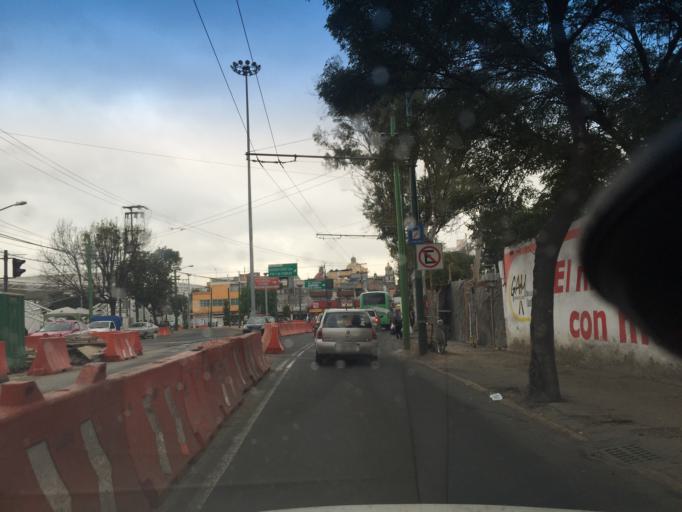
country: MX
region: Mexico City
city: Gustavo A. Madero
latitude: 19.4841
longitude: -99.1128
